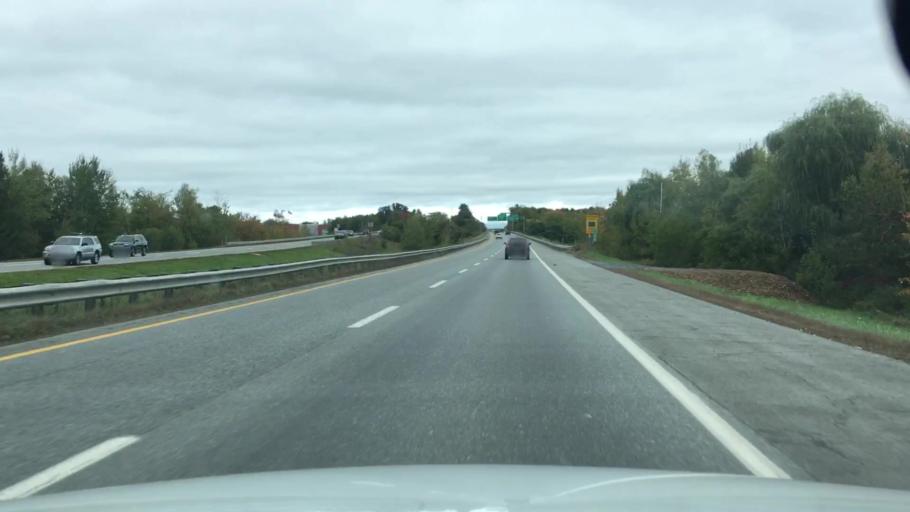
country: US
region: Maine
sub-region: Penobscot County
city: Bangor
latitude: 44.8217
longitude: -68.7649
